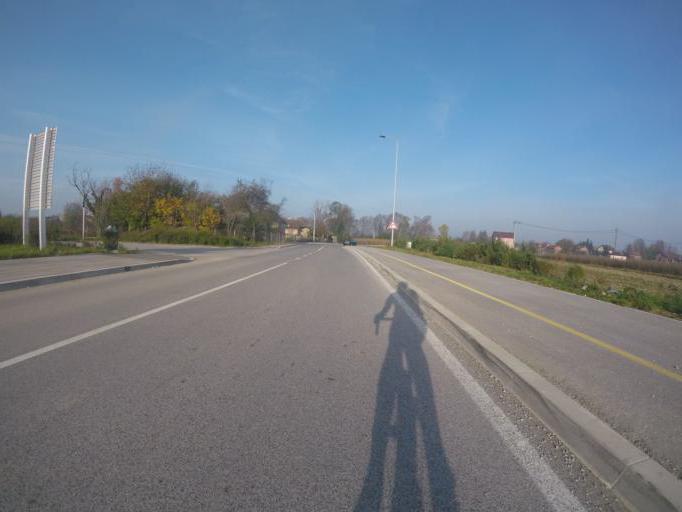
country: HR
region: Zagrebacka
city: Micevec
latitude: 45.7529
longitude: 16.0917
